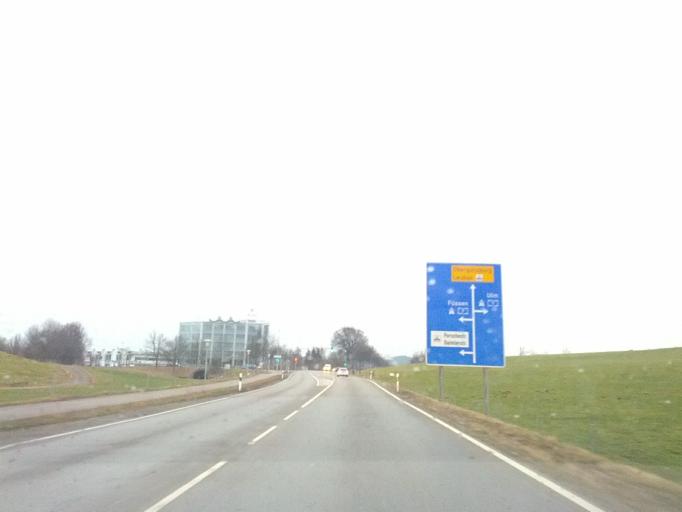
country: DE
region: Bavaria
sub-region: Swabia
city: Kempten (Allgaeu)
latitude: 47.7509
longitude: 10.3268
